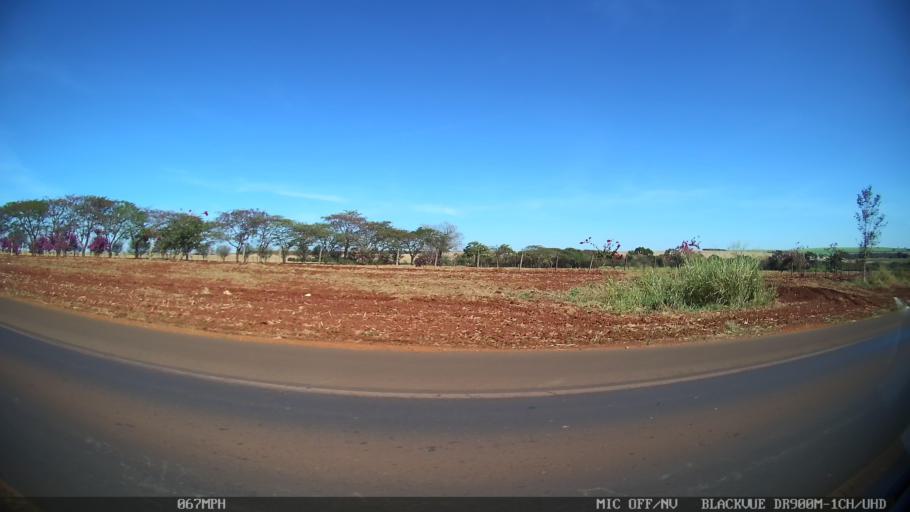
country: BR
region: Sao Paulo
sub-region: Ipua
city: Ipua
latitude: -20.4937
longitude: -47.9829
